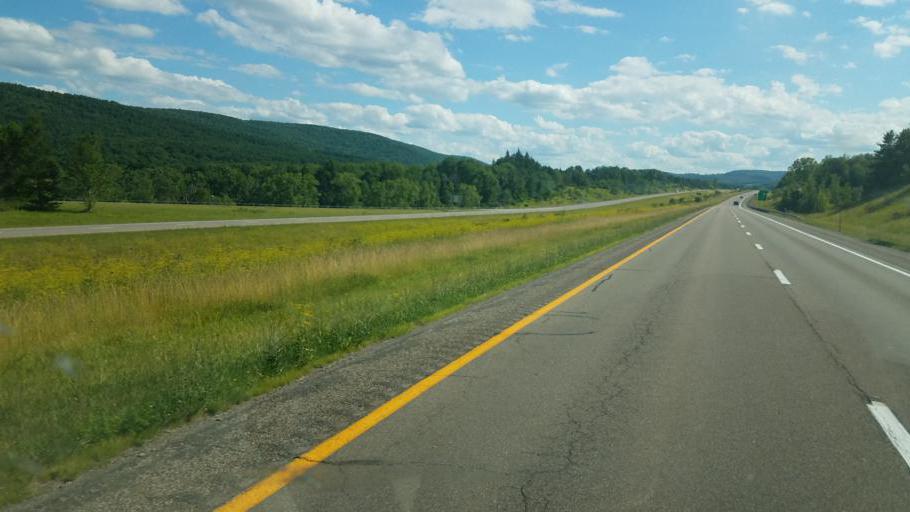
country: US
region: New York
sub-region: Steuben County
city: Hornell
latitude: 42.3414
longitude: -77.7276
